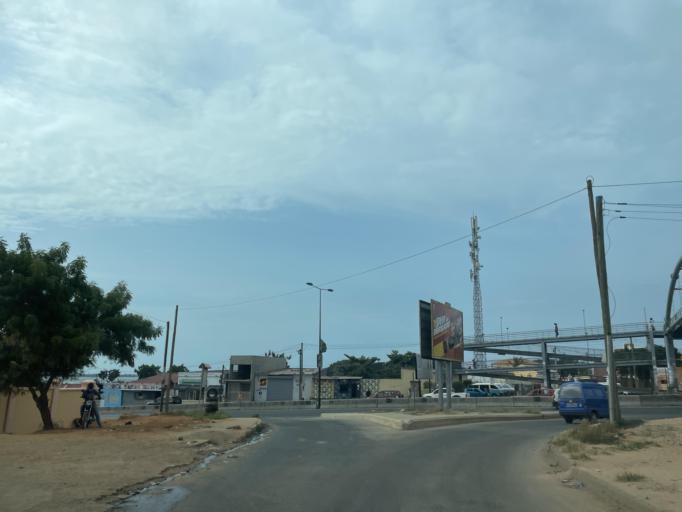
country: AO
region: Luanda
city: Luanda
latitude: -8.9164
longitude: 13.1685
